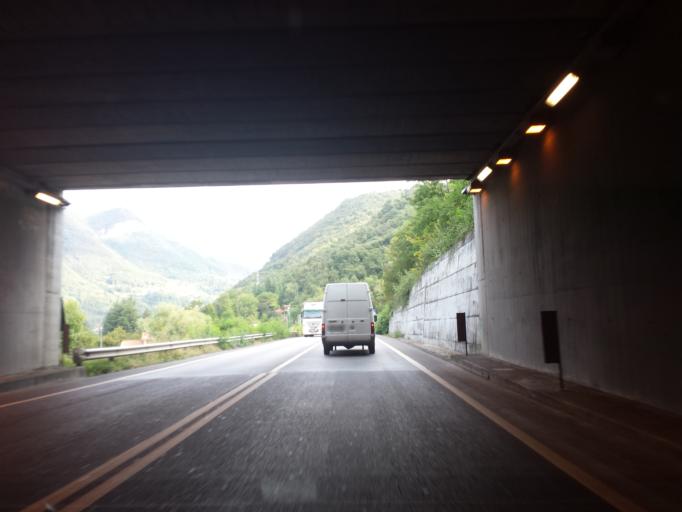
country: IT
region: Lombardy
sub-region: Provincia di Brescia
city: Villanuova sul Clisi
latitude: 45.5904
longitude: 10.4578
